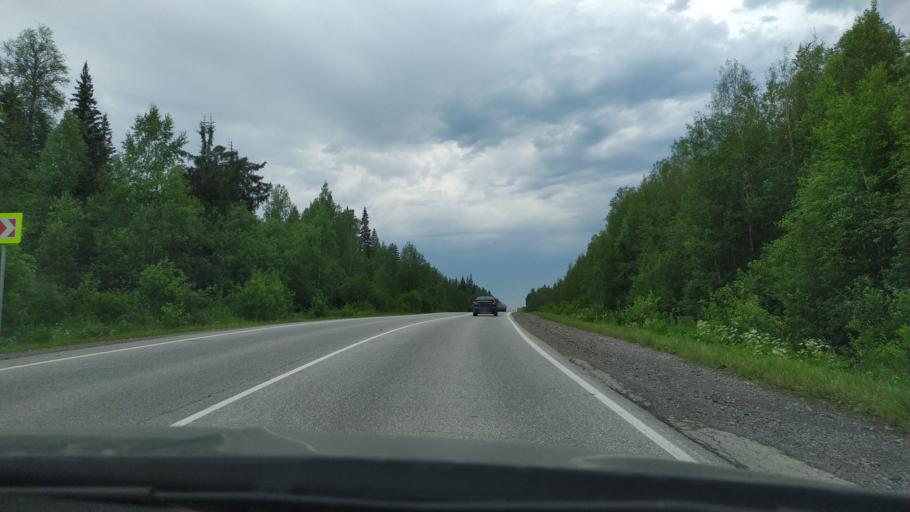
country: RU
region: Perm
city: Chusovoy
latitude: 58.3705
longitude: 57.8869
